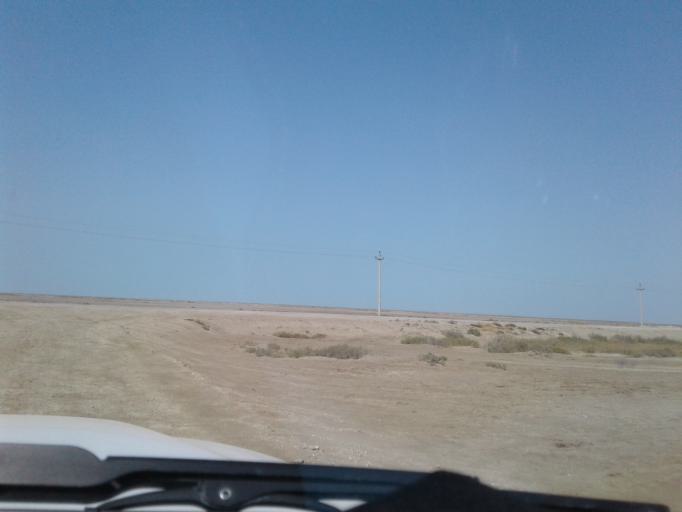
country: IR
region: Golestan
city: Gomishan
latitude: 37.8196
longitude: 53.9201
